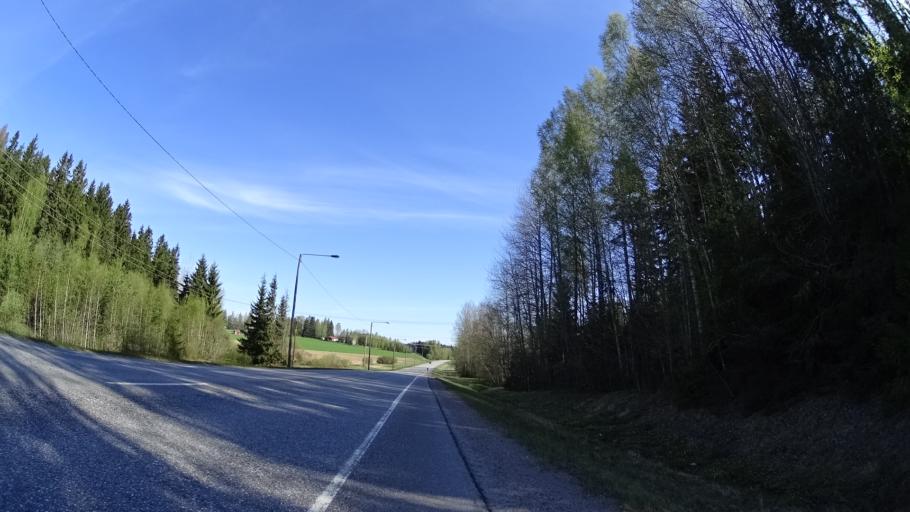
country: FI
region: Uusimaa
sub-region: Helsinki
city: Nurmijaervi
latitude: 60.3886
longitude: 24.8087
